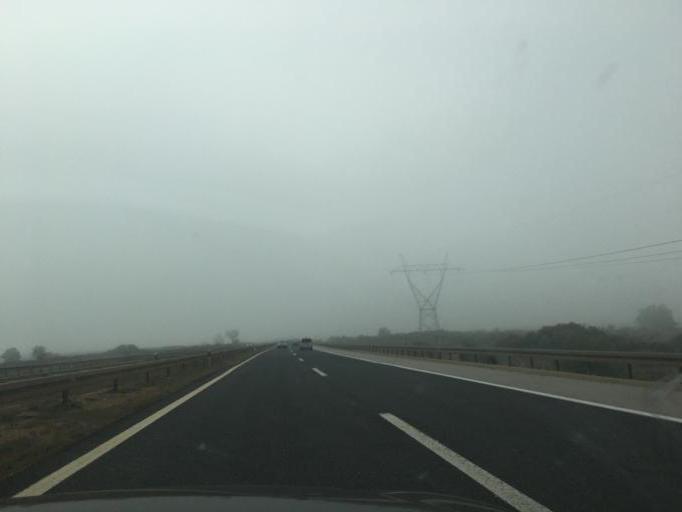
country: HR
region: Licko-Senjska
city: Gospic
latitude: 44.6087
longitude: 15.4400
